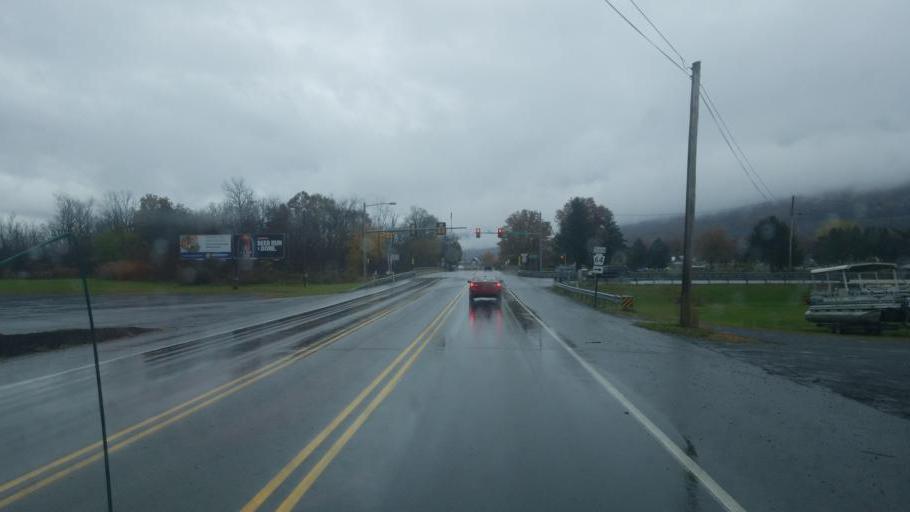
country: US
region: Pennsylvania
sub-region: Clinton County
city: Mill Hall
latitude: 41.1130
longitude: -77.4889
